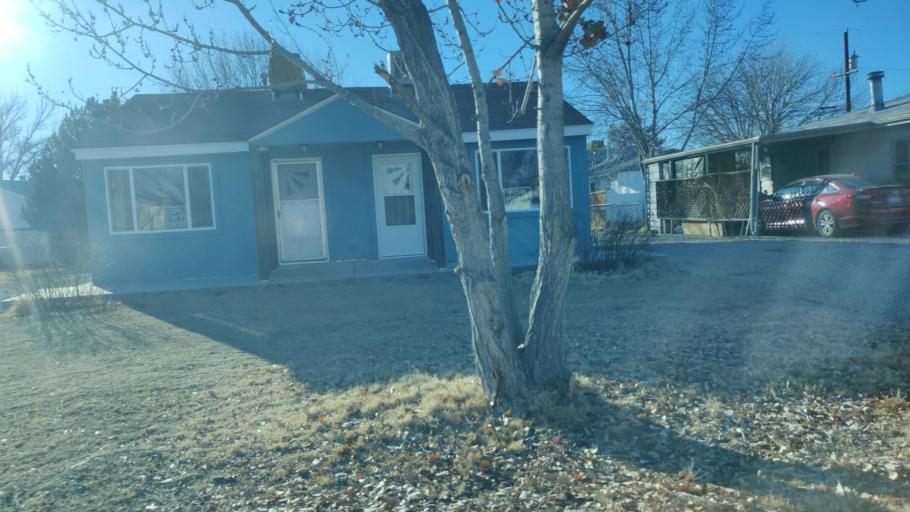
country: US
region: Colorado
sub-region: Mesa County
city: Grand Junction
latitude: 39.0869
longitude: -108.5351
